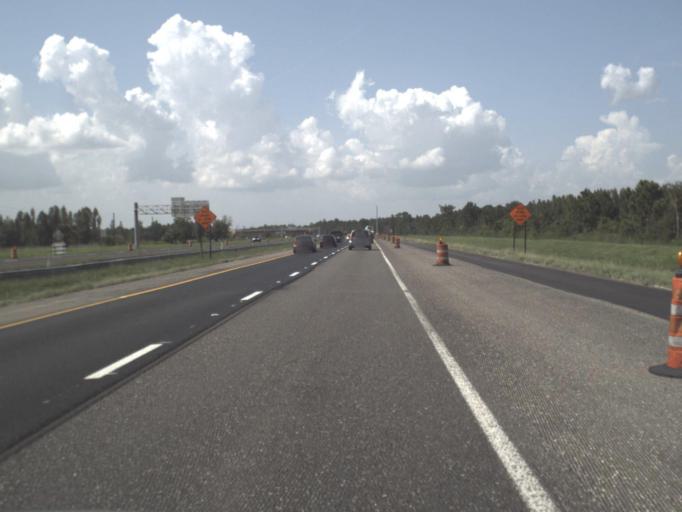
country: US
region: Florida
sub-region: Hillsborough County
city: Pebble Creek
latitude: 28.1332
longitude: -82.3780
